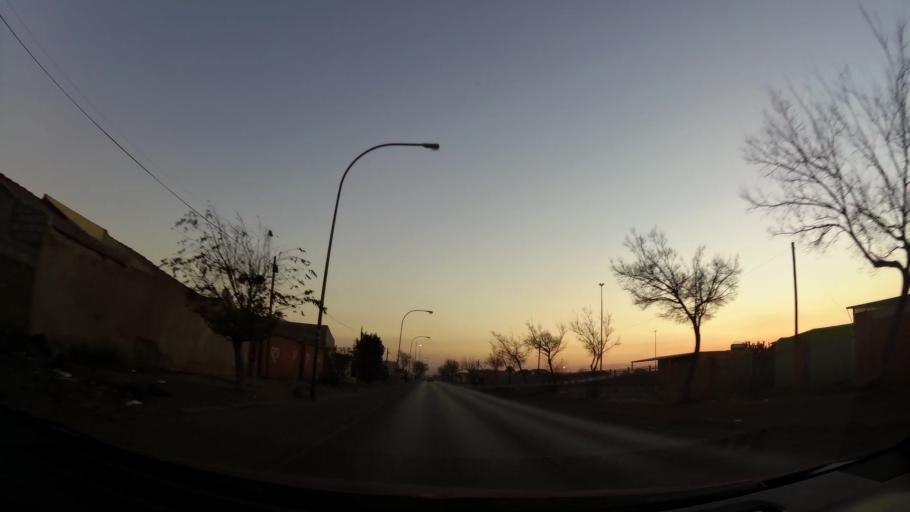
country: ZA
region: Gauteng
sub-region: City of Johannesburg Metropolitan Municipality
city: Soweto
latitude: -26.2319
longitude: 27.8351
